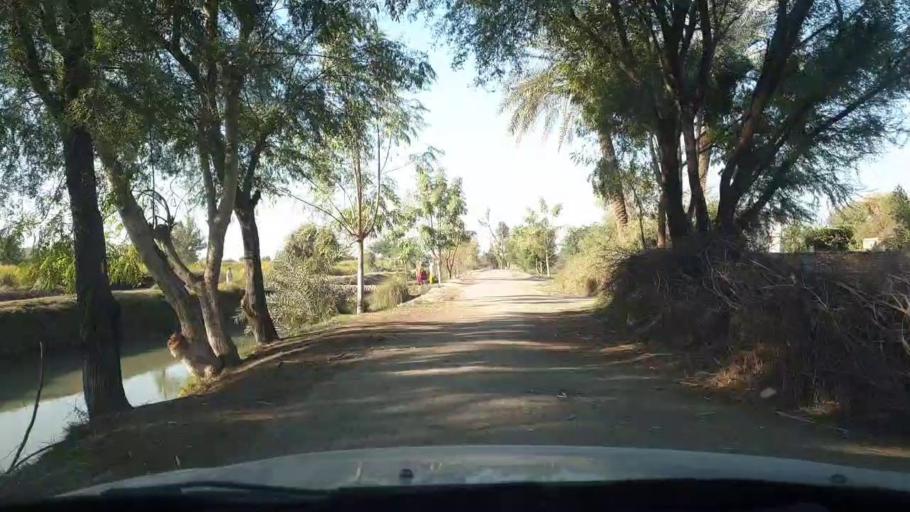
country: PK
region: Sindh
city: Adilpur
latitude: 27.9346
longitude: 69.2607
